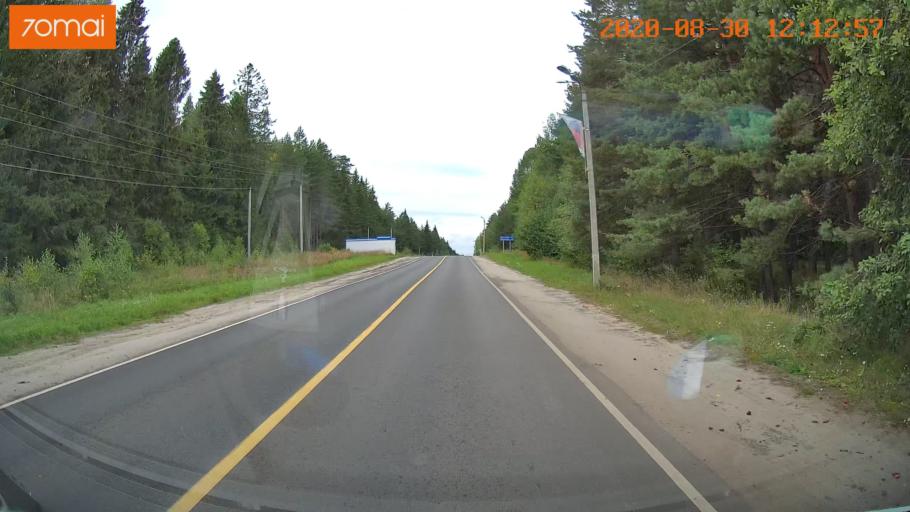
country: RU
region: Ivanovo
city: Yur'yevets
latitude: 57.3119
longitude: 43.0879
